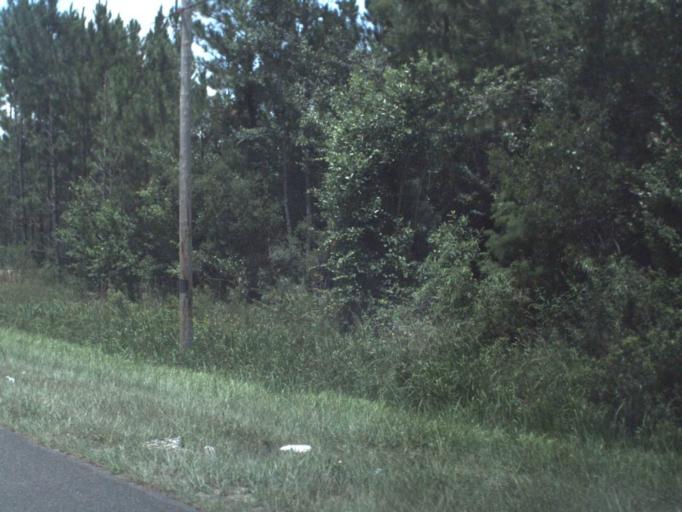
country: US
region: Florida
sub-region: Clay County
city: Keystone Heights
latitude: 29.8303
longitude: -82.0616
